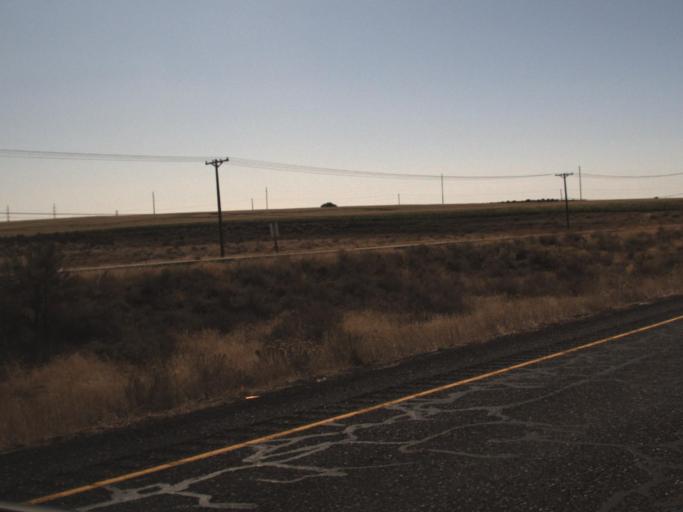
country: US
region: Washington
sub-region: Franklin County
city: Basin City
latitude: 46.4366
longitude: -119.0229
